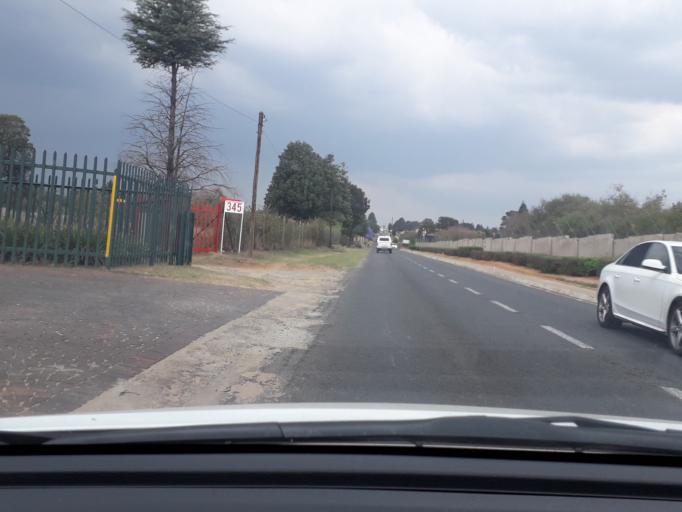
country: ZA
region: Gauteng
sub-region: West Rand District Municipality
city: Muldersdriseloop
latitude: -26.0623
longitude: 27.9258
